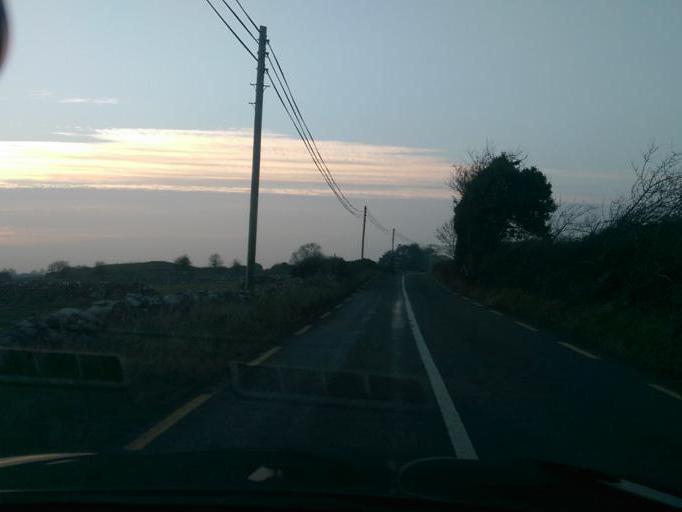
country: IE
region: Connaught
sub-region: County Galway
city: Loughrea
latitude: 53.2153
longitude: -8.6139
